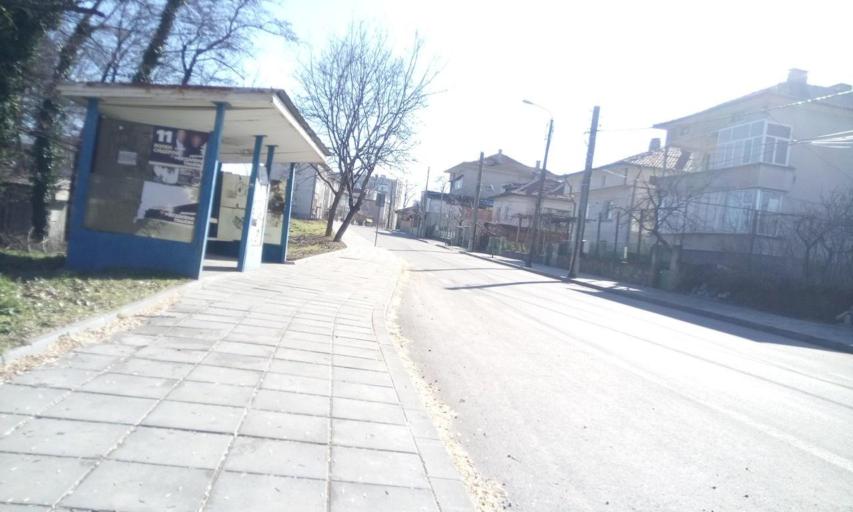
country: BG
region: Plovdiv
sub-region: Obshtina Khisarya
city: Khisarya
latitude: 42.5079
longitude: 24.7136
